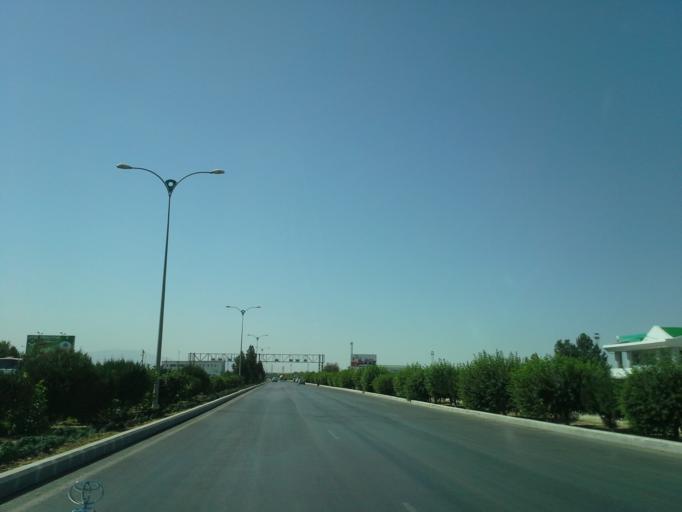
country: TM
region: Ahal
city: Annau
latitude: 37.9086
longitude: 58.5075
